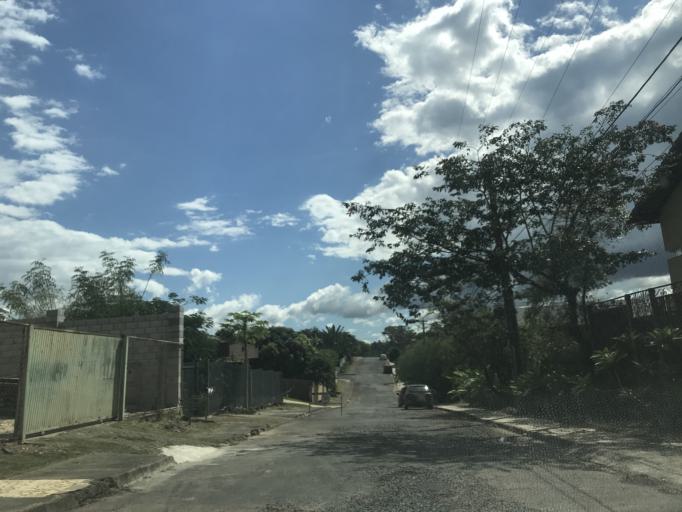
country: BR
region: Federal District
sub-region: Brasilia
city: Brasilia
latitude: -15.8667
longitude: -47.7518
